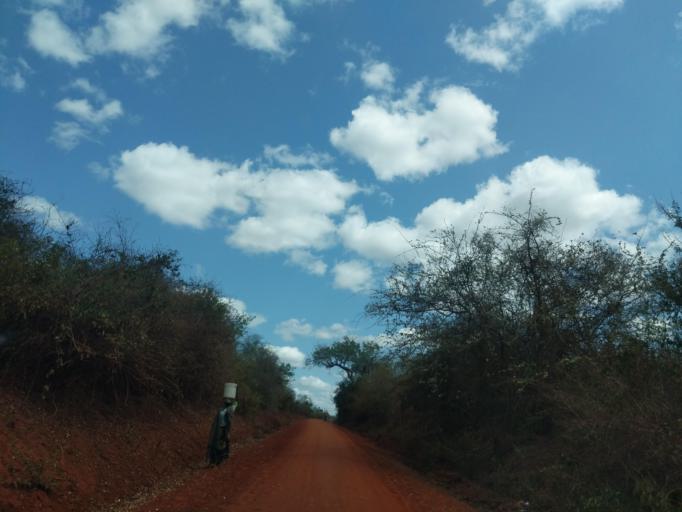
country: TZ
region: Tanga
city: Chanika
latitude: -5.5167
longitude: 38.3552
